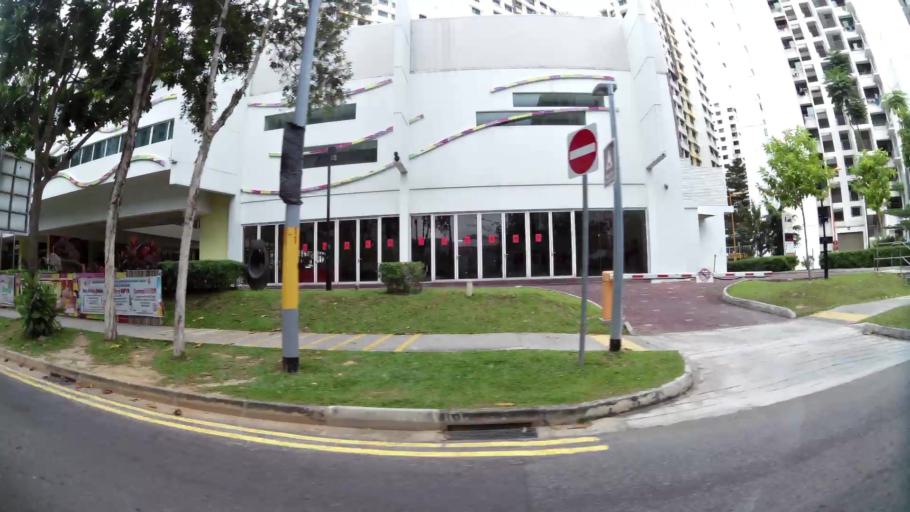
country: MY
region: Johor
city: Kampung Pasir Gudang Baru
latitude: 1.3932
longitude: 103.9136
